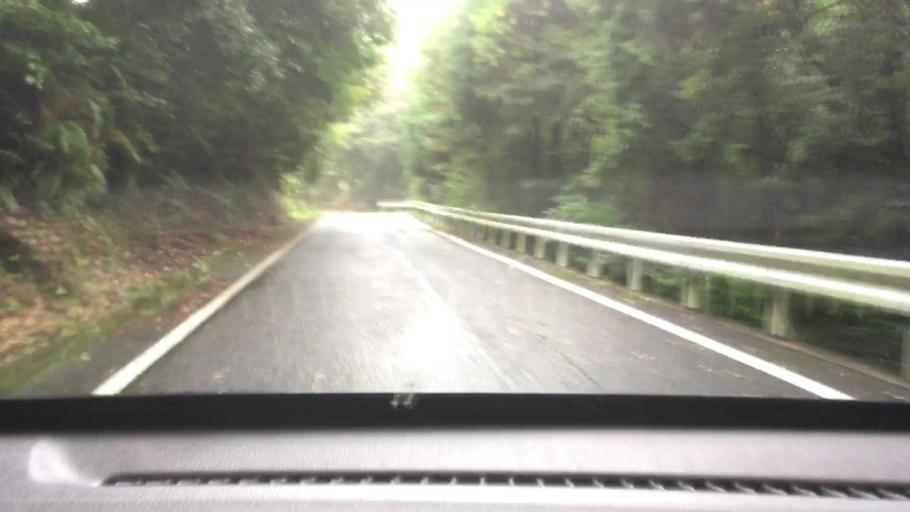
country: JP
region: Nagasaki
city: Togitsu
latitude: 32.9187
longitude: 129.7262
